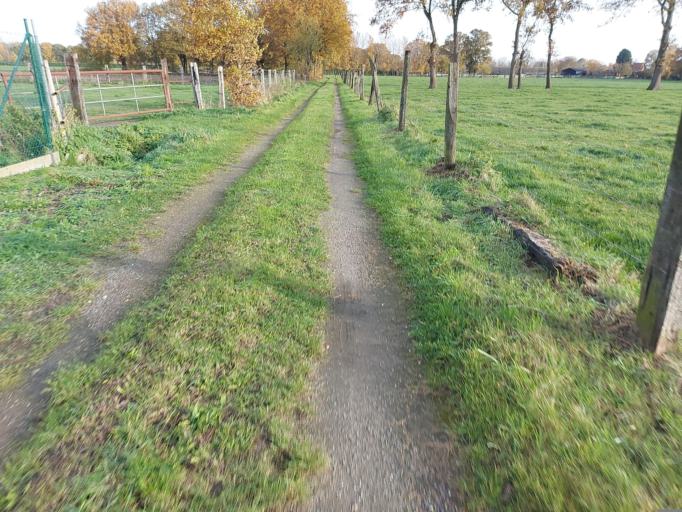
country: BE
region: Flanders
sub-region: Provincie Antwerpen
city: Geel
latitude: 51.1546
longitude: 4.9288
